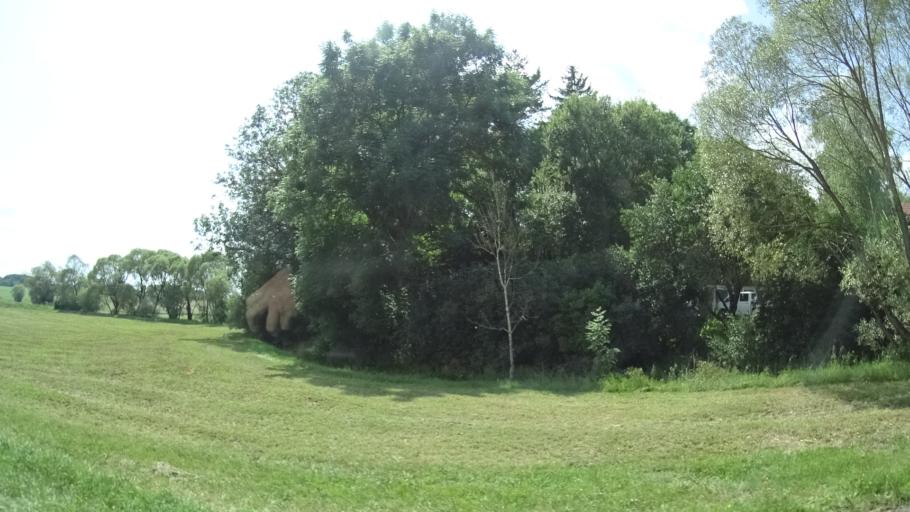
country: DE
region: Thuringia
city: Veilsdorf
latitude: 50.4038
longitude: 10.8143
